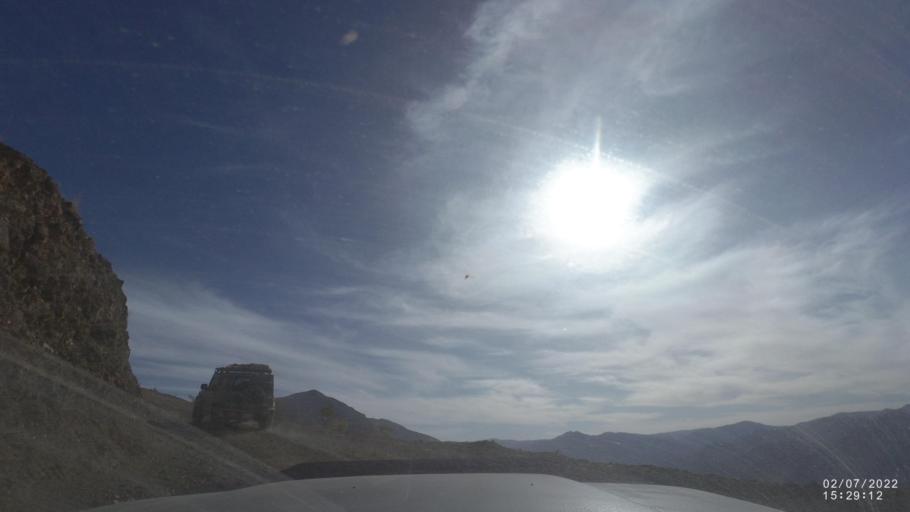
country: BO
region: Cochabamba
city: Irpa Irpa
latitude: -17.8789
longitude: -66.4130
